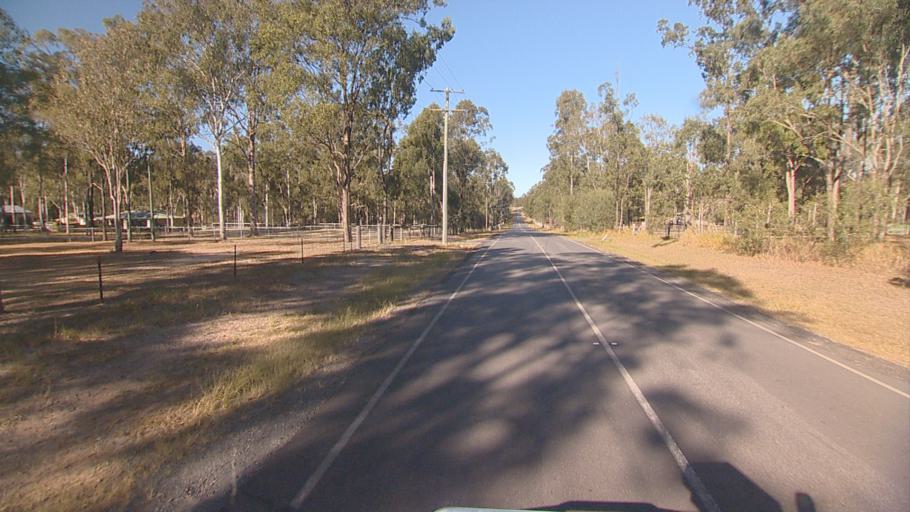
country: AU
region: Queensland
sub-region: Logan
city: North Maclean
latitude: -27.8154
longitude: 152.9886
